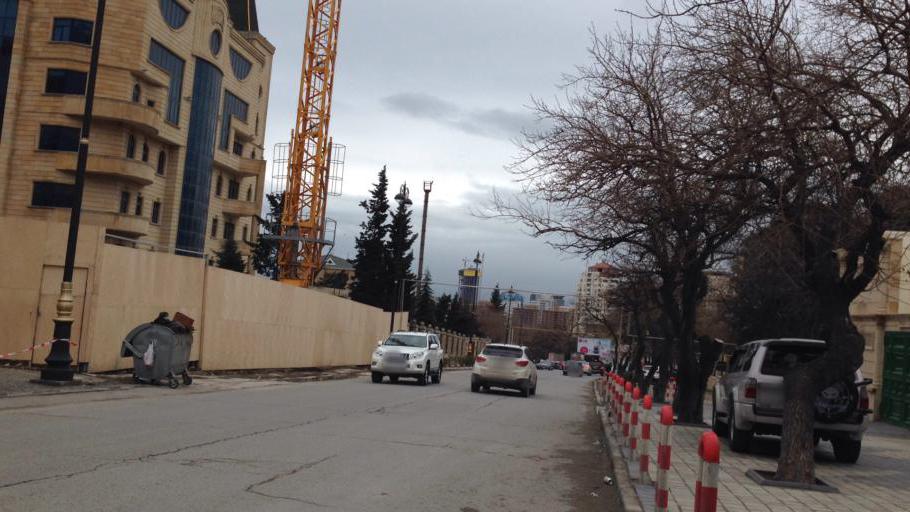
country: AZ
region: Baki
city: Baku
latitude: 40.3906
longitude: 49.8494
